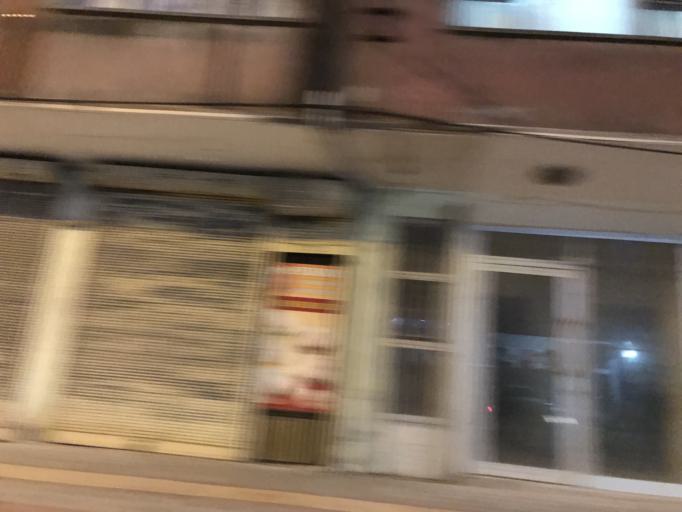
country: TR
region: Hatay
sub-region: Antakya Ilcesi
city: Antakya
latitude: 36.1992
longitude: 36.1504
